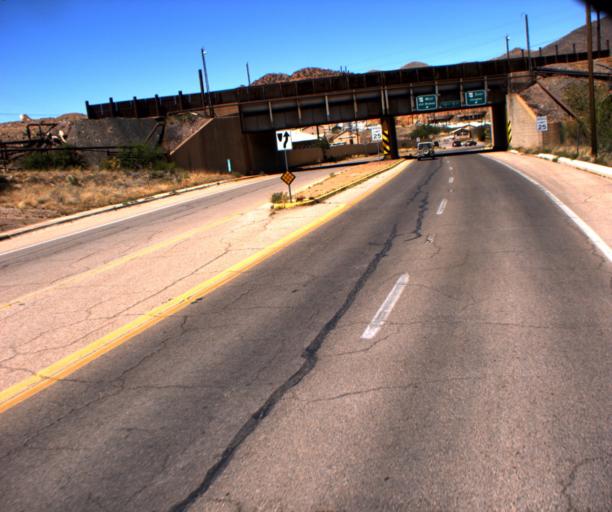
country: US
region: Arizona
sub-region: Cochise County
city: Bisbee
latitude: 31.4255
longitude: -109.8933
